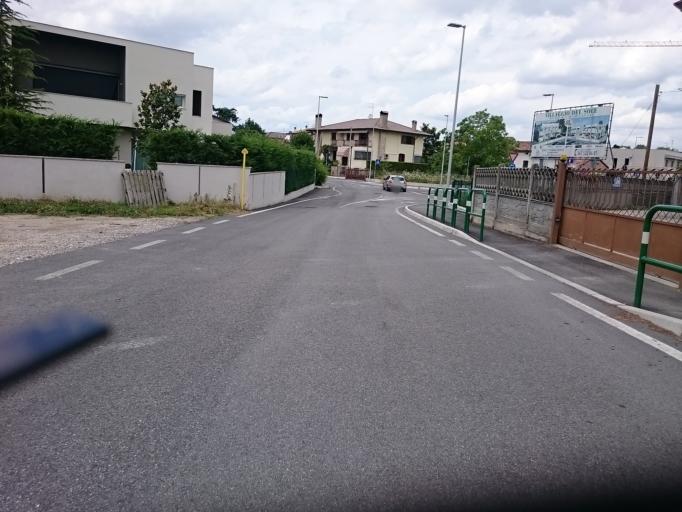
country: IT
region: Veneto
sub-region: Provincia di Padova
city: Caselle
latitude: 45.4167
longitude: 11.8220
